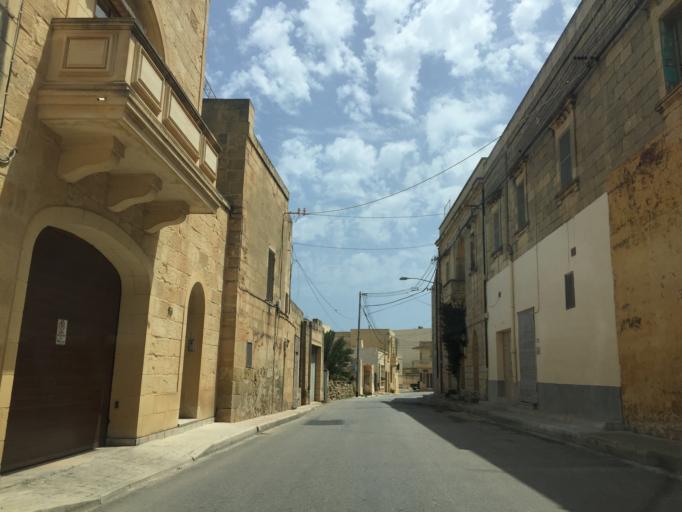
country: MT
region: Ix-Xaghra
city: Xaghra
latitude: 36.0540
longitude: 14.2703
